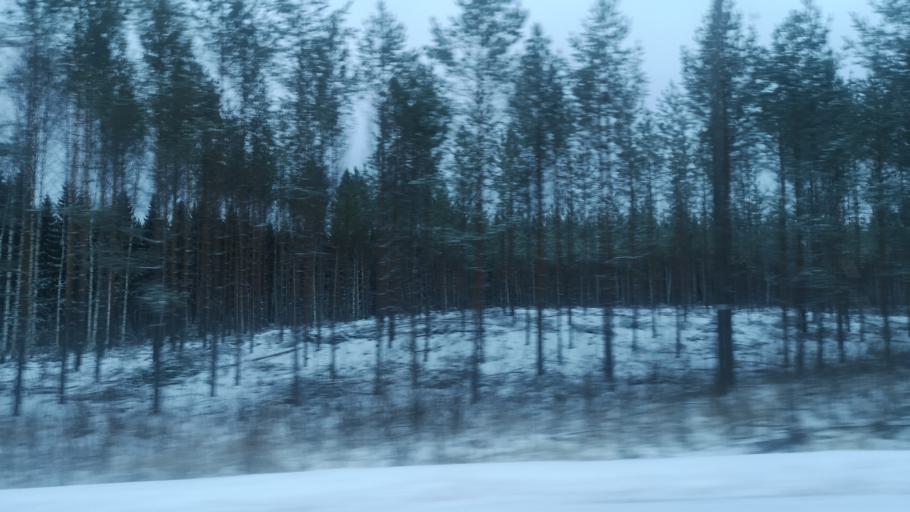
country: FI
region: Southern Savonia
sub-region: Savonlinna
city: Enonkoski
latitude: 62.0996
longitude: 28.6574
